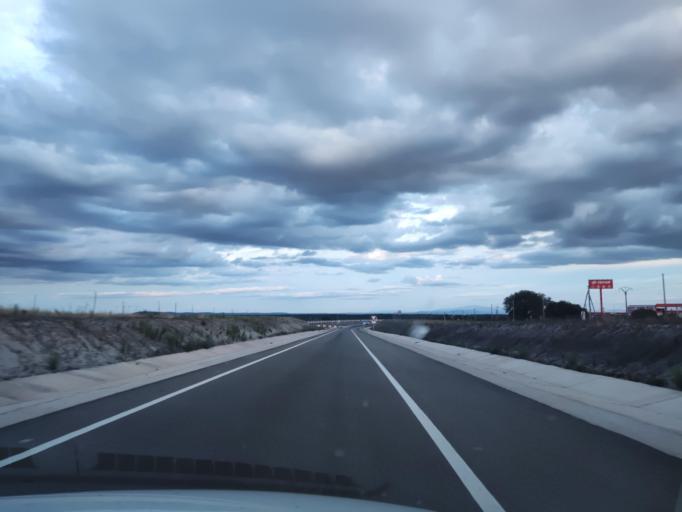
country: ES
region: Castille and Leon
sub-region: Provincia de Salamanca
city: Fuentes de Onoro
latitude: 40.5932
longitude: -6.7960
